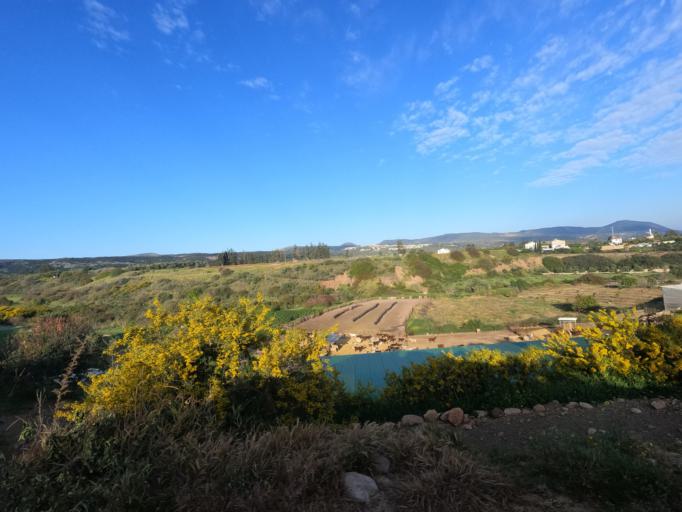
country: CY
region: Pafos
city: Polis
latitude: 35.0314
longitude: 32.3988
